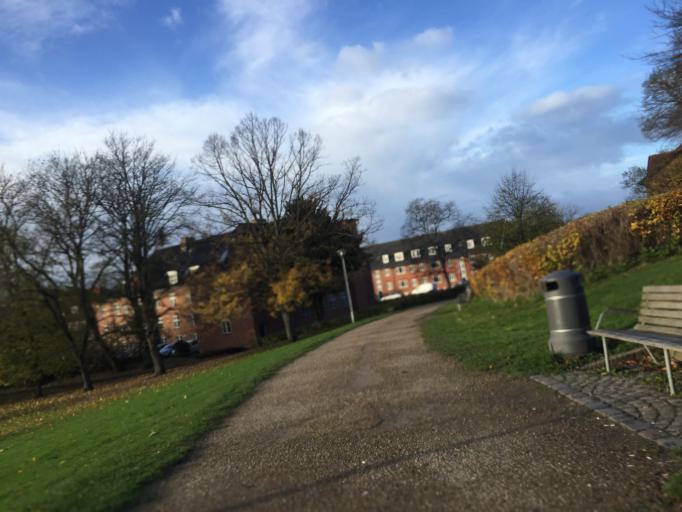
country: DK
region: Zealand
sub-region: Ringsted Kommune
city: Ringsted
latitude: 55.4448
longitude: 11.7872
